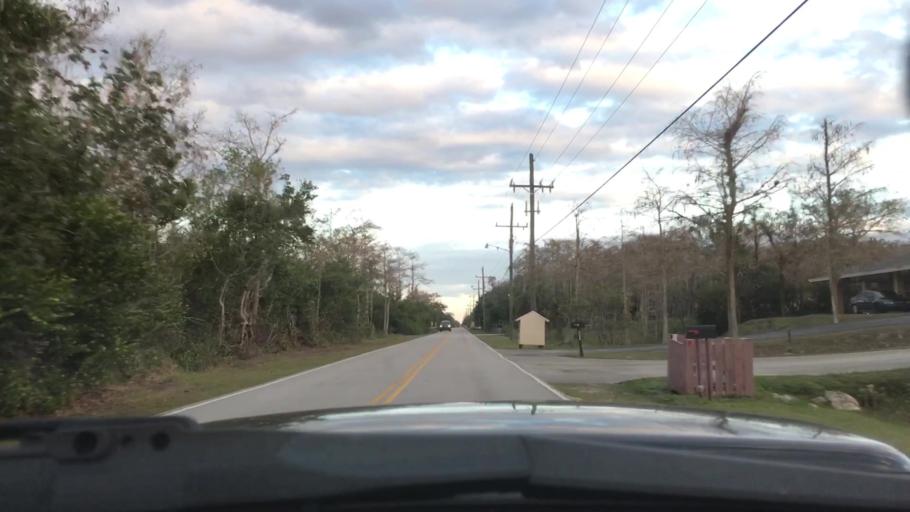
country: US
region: Florida
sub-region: Miami-Dade County
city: Kendall West
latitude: 25.7607
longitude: -80.8470
